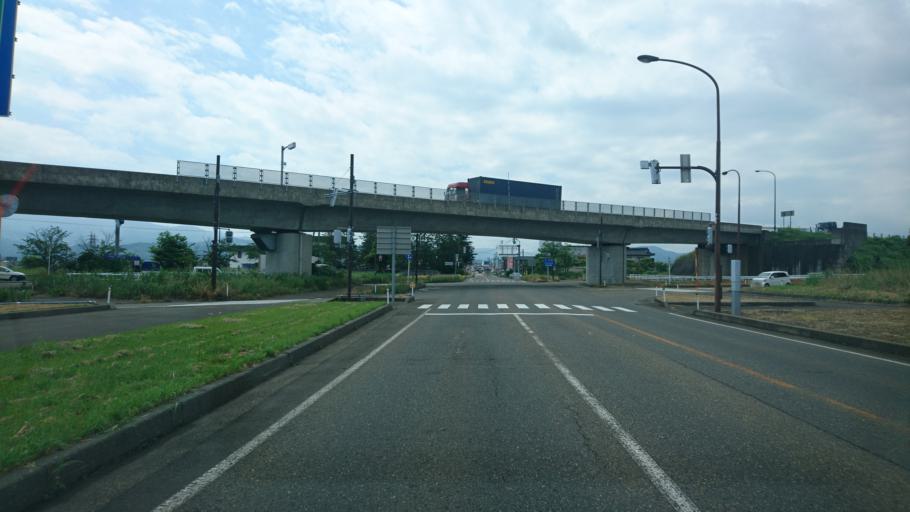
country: JP
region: Niigata
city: Arai
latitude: 37.0603
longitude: 138.2595
